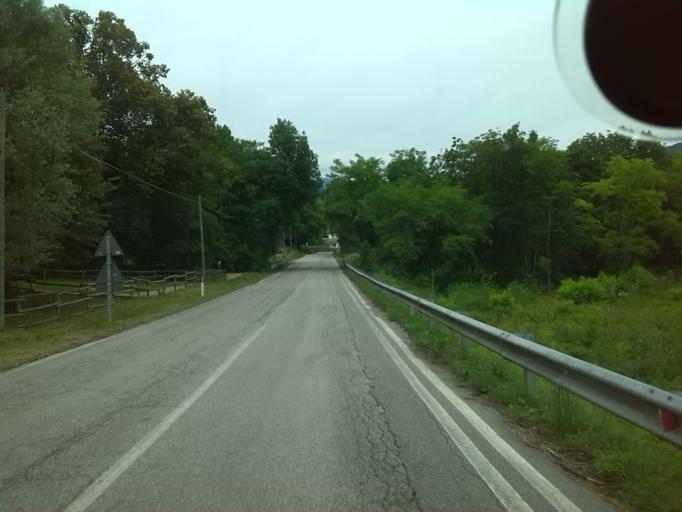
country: IT
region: Friuli Venezia Giulia
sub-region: Provincia di Udine
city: San Pietro al Natisone
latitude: 46.1275
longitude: 13.4973
